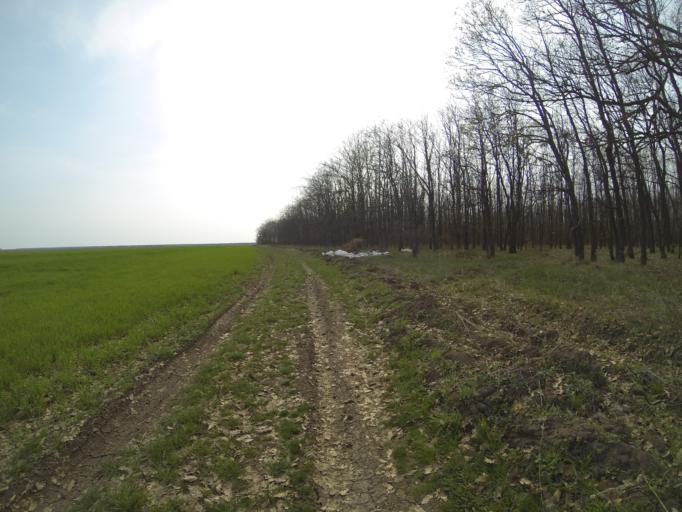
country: RO
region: Dolj
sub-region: Comuna Breasta
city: Breasta
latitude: 44.2734
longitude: 23.6676
